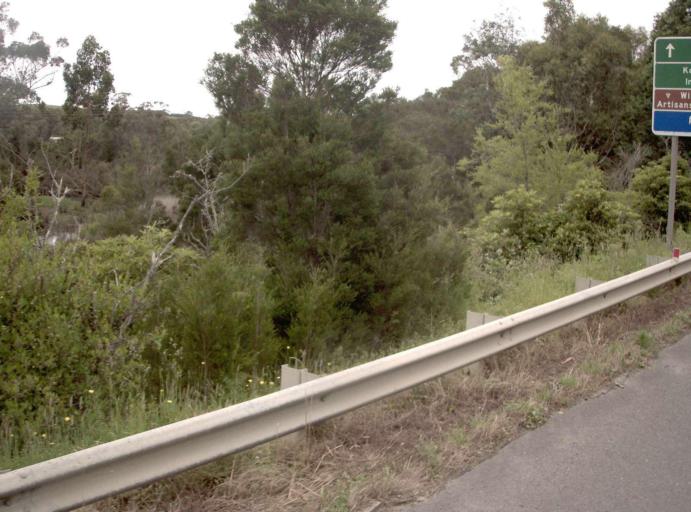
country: AU
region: Victoria
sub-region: Bass Coast
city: North Wonthaggi
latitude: -38.5435
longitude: 145.9471
